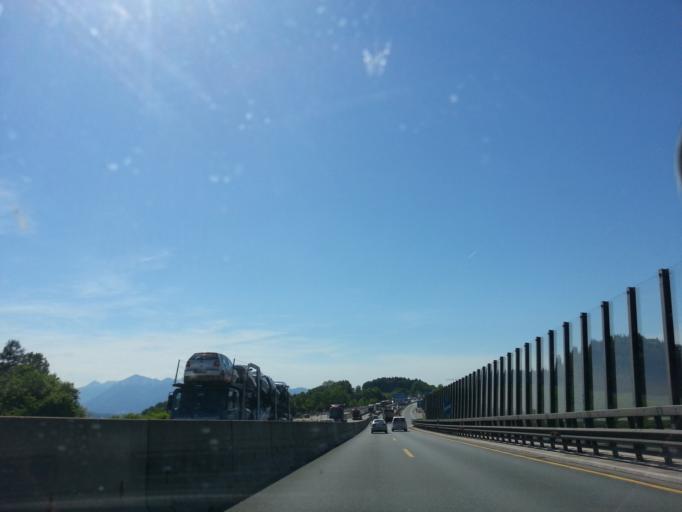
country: DE
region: Bavaria
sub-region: Upper Bavaria
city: Bergen
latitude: 47.8285
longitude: 12.6018
